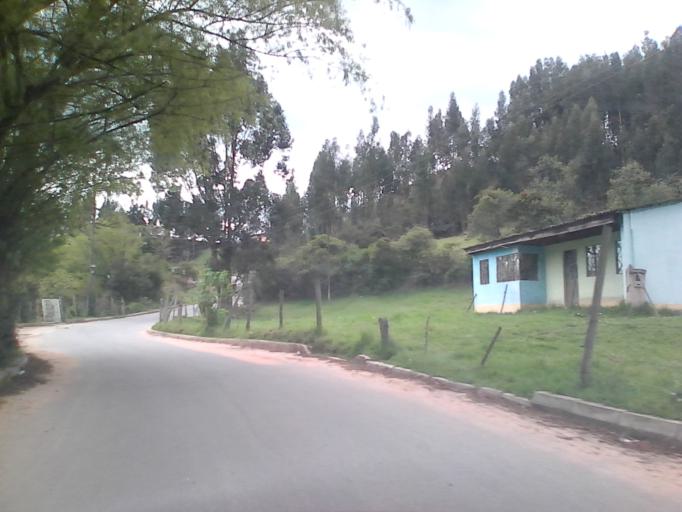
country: CO
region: Boyaca
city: Duitama
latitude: 5.8282
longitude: -73.0606
